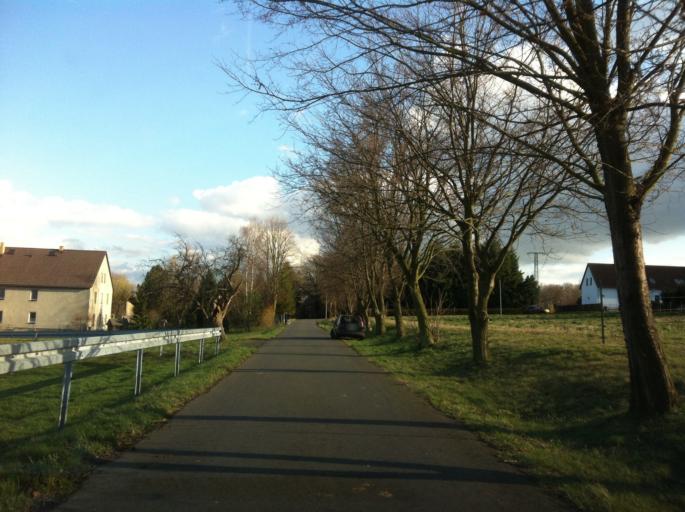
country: DE
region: Saxony
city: Trebsen
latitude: 51.3109
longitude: 12.7385
